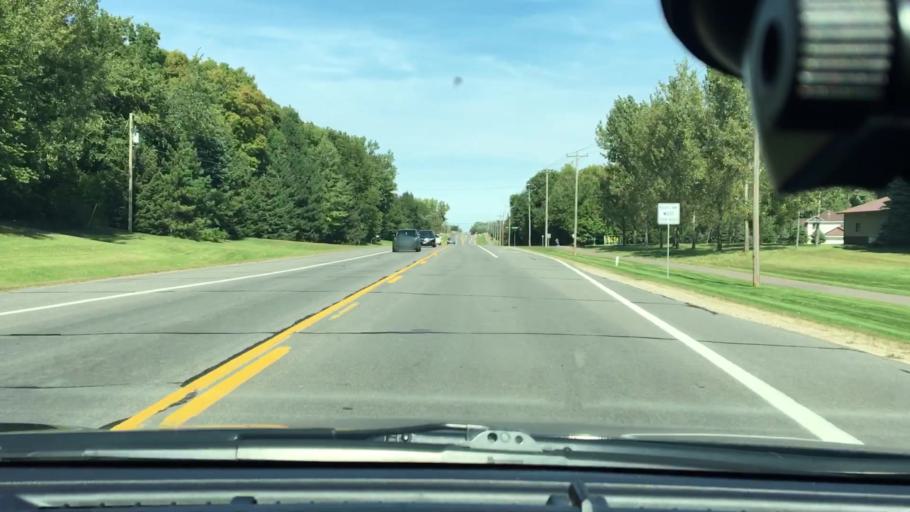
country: US
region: Minnesota
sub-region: Wright County
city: Hanover
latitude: 45.1671
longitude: -93.6659
